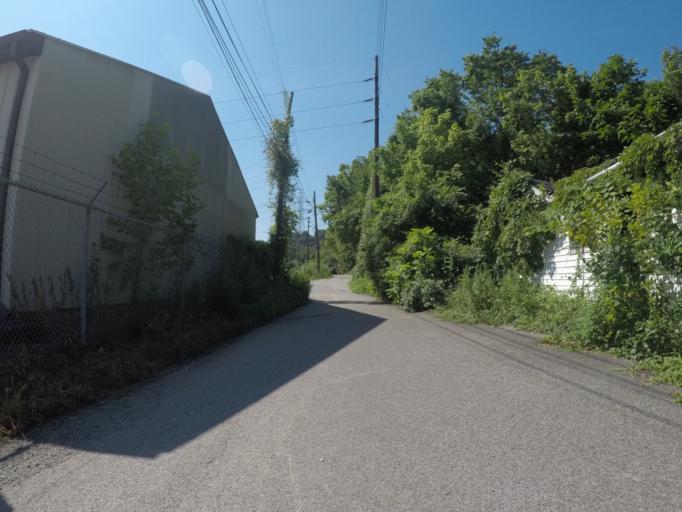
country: US
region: West Virginia
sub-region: Cabell County
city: Huntington
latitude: 38.4058
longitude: -82.4807
